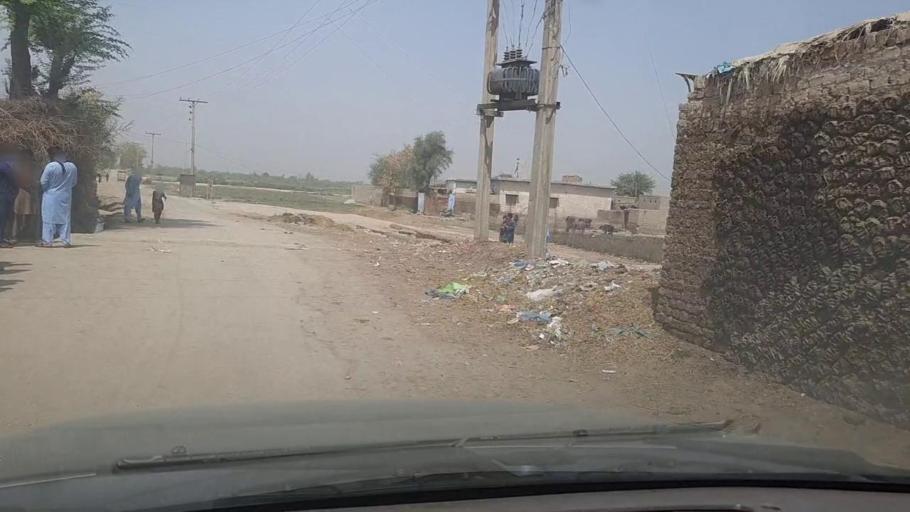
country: PK
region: Sindh
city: Madeji
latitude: 27.7981
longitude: 68.4212
